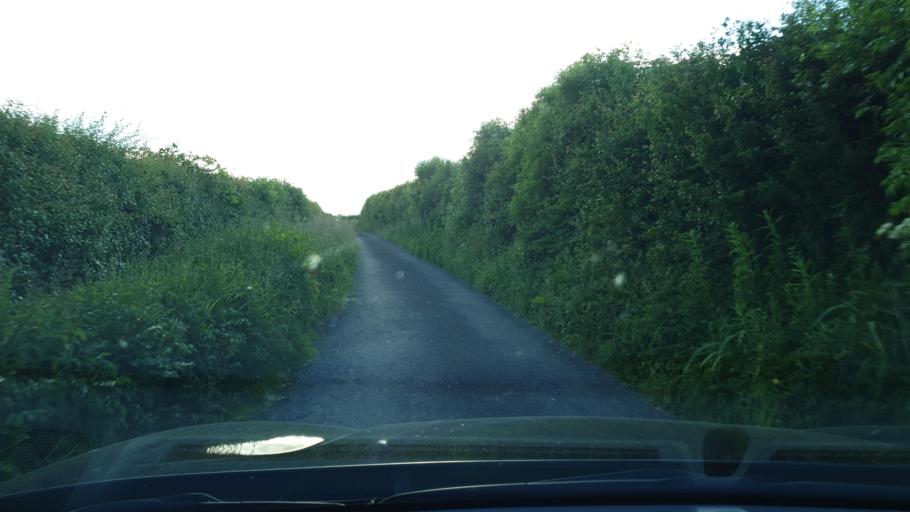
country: IE
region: Leinster
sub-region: Fingal County
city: Blanchardstown
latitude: 53.4450
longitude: -6.3938
